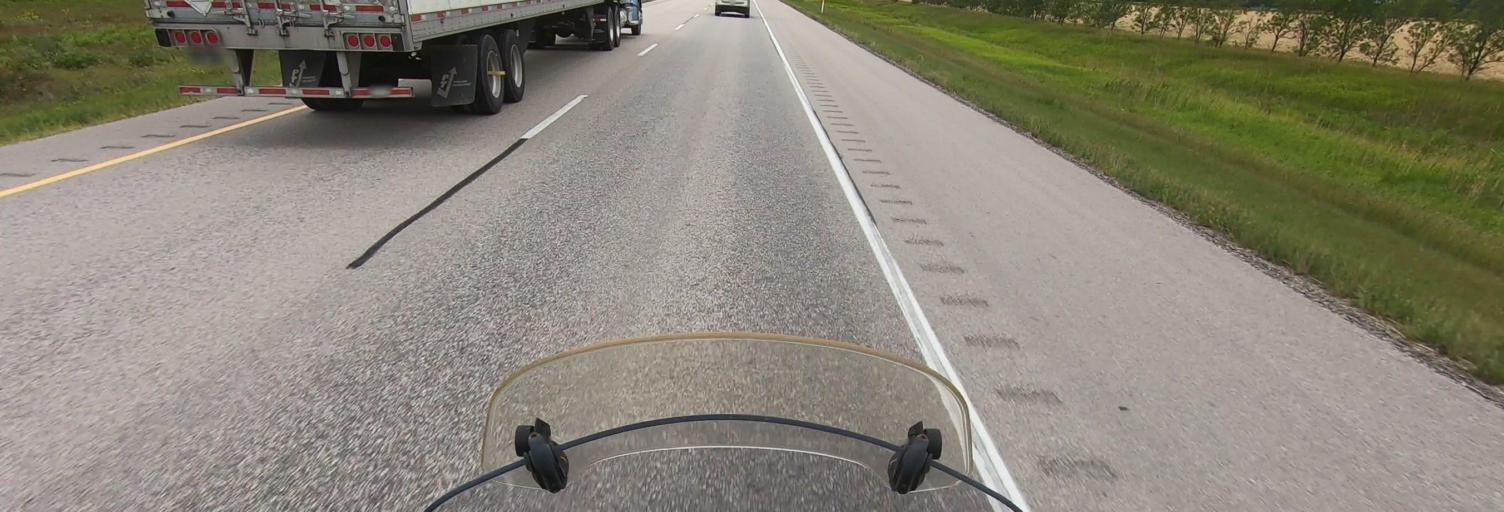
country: CA
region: Manitoba
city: Portage la Prairie
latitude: 49.9480
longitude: -97.9784
